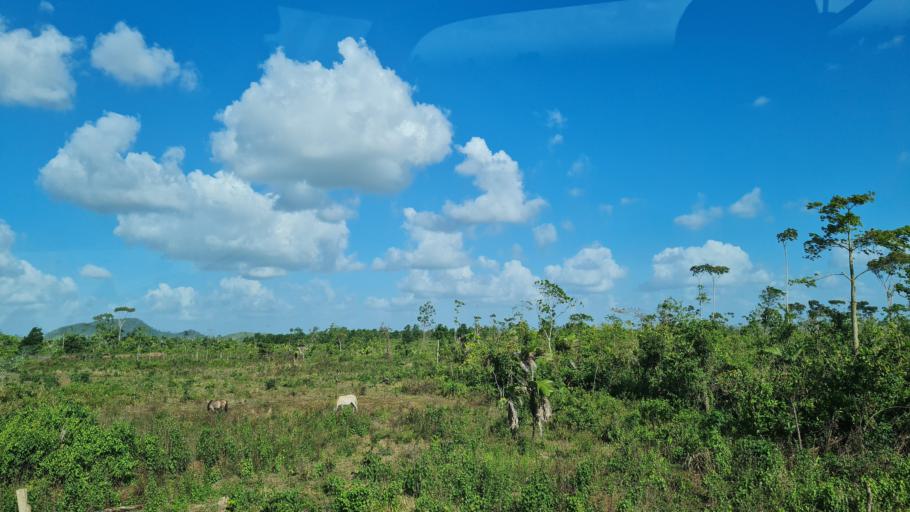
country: NI
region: Atlantico Norte (RAAN)
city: Bonanza
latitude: 13.9949
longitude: -84.1708
